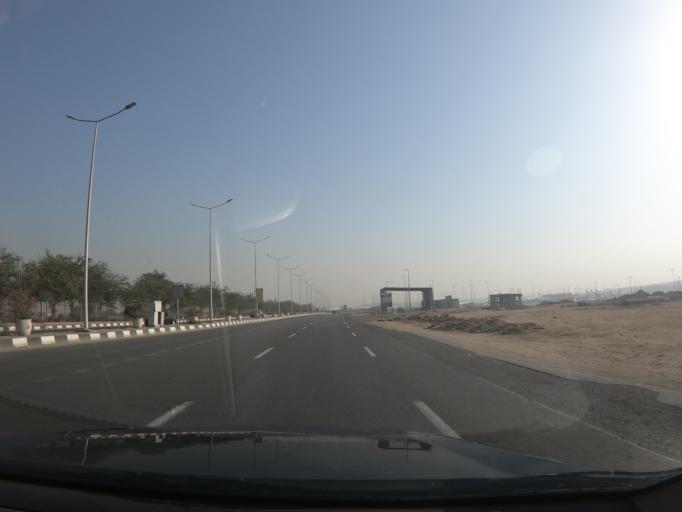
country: EG
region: Muhafazat al Qalyubiyah
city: Al Khankah
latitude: 30.0991
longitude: 31.3856
